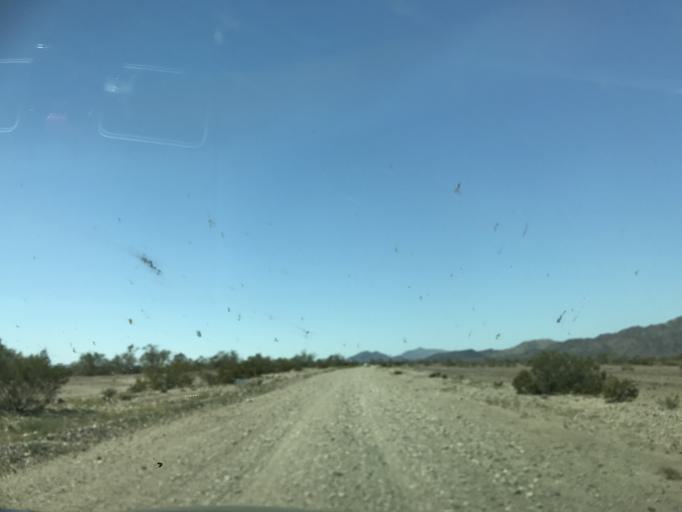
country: US
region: California
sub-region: Riverside County
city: Mesa Verde
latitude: 33.4812
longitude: -114.9263
